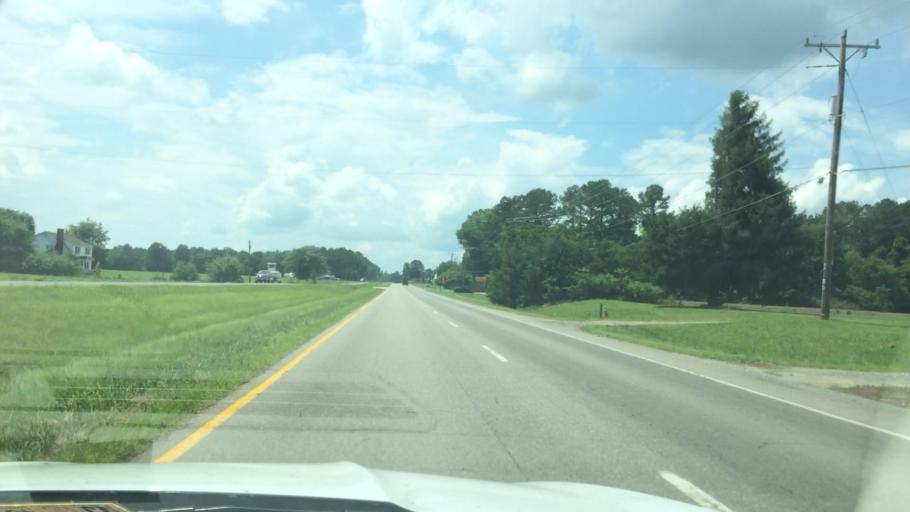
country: US
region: Virginia
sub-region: King William County
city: West Point
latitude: 37.5451
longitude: -76.7095
